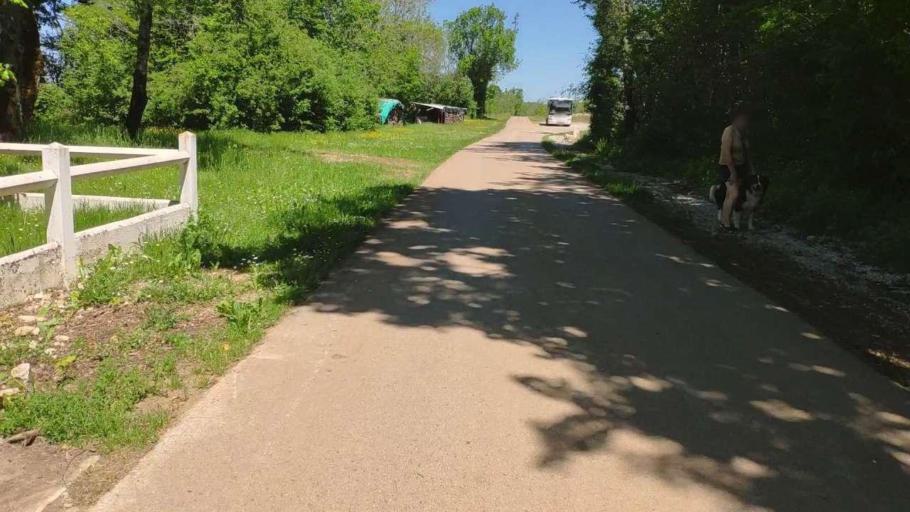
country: FR
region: Franche-Comte
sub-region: Departement du Jura
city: Perrigny
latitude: 46.7205
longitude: 5.6454
